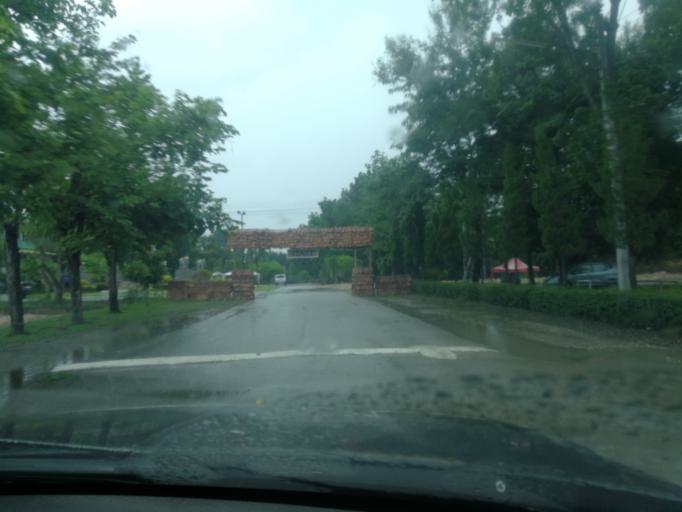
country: TH
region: Chiang Mai
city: San Pa Tong
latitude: 18.6474
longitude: 98.8489
